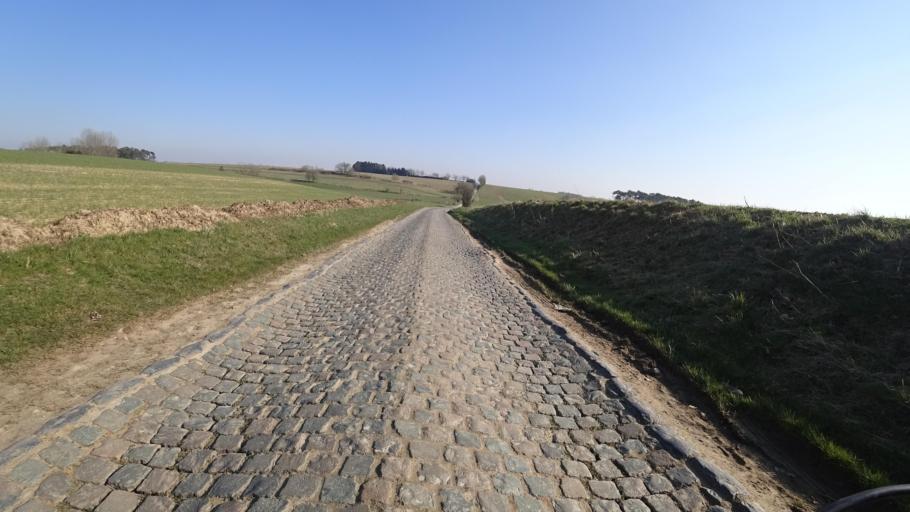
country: BE
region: Wallonia
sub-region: Province du Brabant Wallon
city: Mont-Saint-Guibert
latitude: 50.6072
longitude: 4.5934
